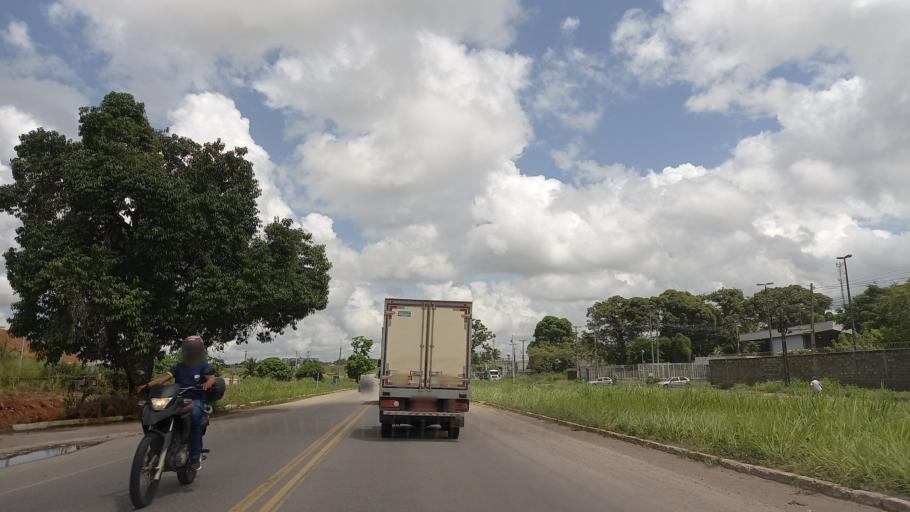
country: BR
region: Pernambuco
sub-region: Cabo De Santo Agostinho
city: Cabo
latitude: -8.2487
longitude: -35.0019
